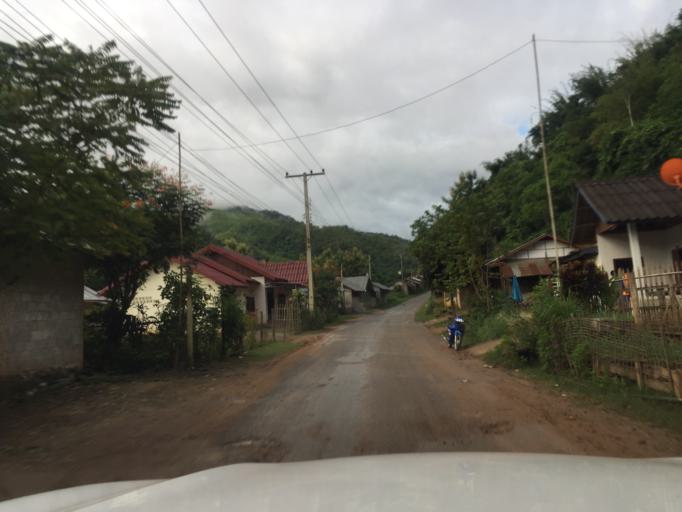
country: LA
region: Phongsali
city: Khoa
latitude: 21.0994
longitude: 102.2529
